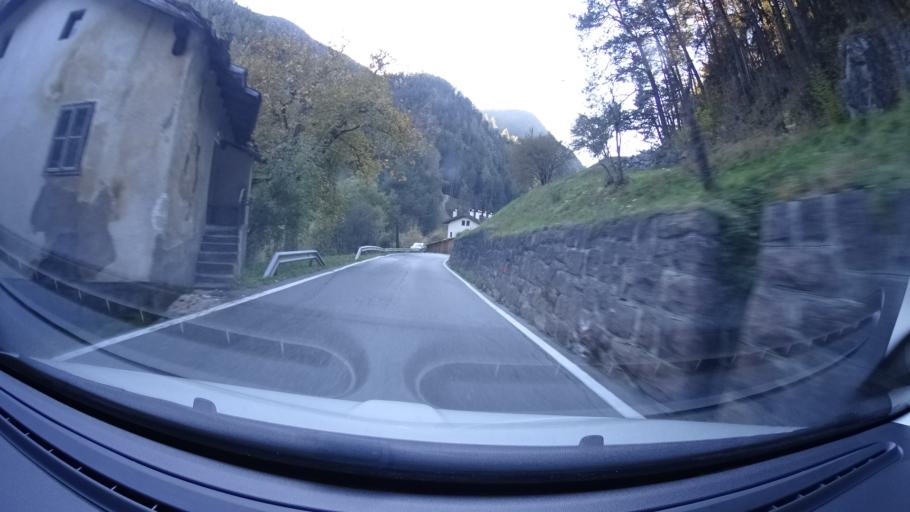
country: IT
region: Trentino-Alto Adige
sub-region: Bolzano
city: Laion
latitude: 46.5952
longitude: 11.5787
